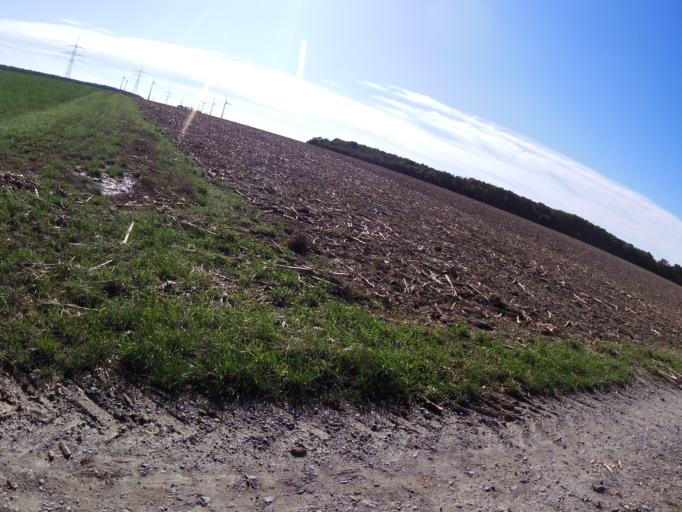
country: DE
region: Bavaria
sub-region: Regierungsbezirk Unterfranken
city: Theilheim
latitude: 49.7483
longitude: 10.0502
